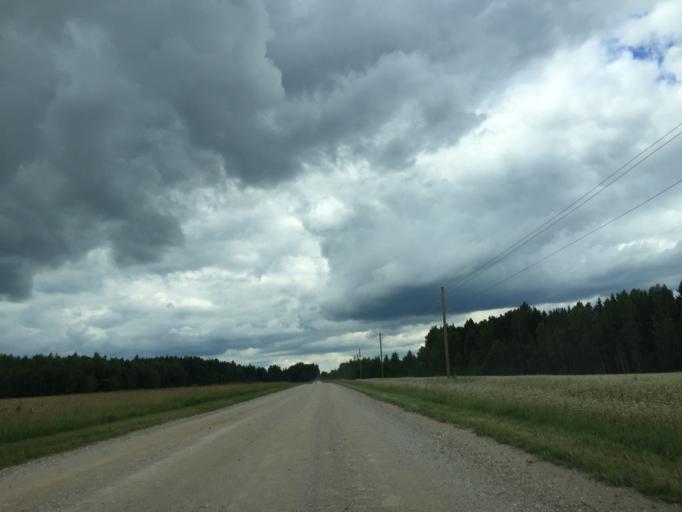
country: LV
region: Malpils
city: Malpils
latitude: 56.8655
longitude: 25.0127
